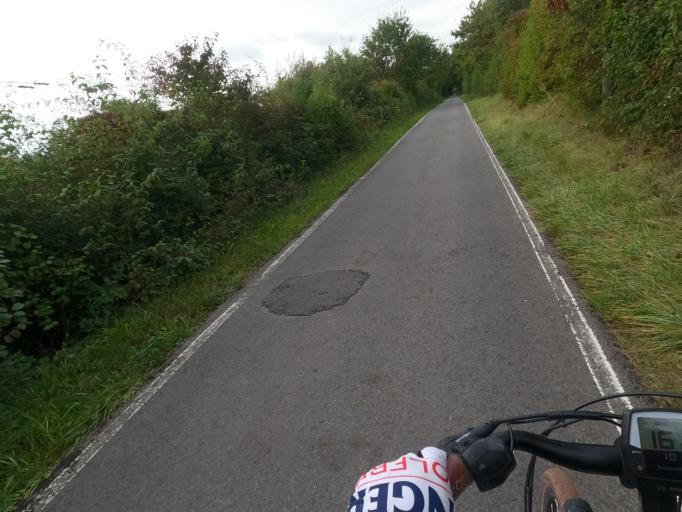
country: CH
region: Thurgau
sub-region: Kreuzlingen District
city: Ermatingen
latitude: 47.6977
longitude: 9.1111
